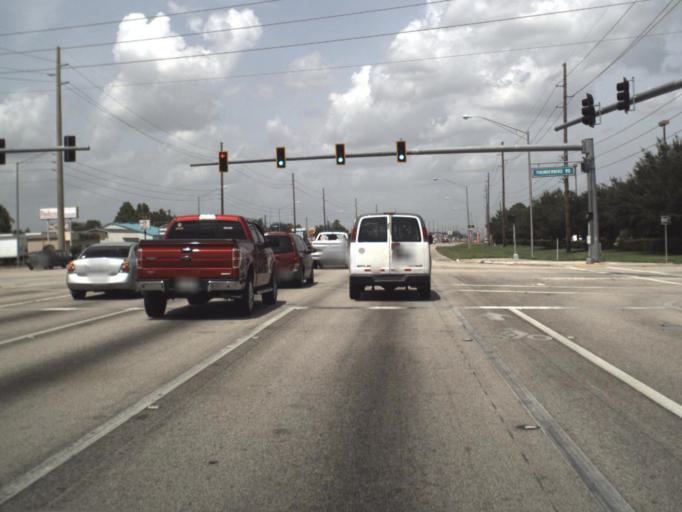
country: US
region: Florida
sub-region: Highlands County
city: Sebring
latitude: 27.4996
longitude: -81.4892
